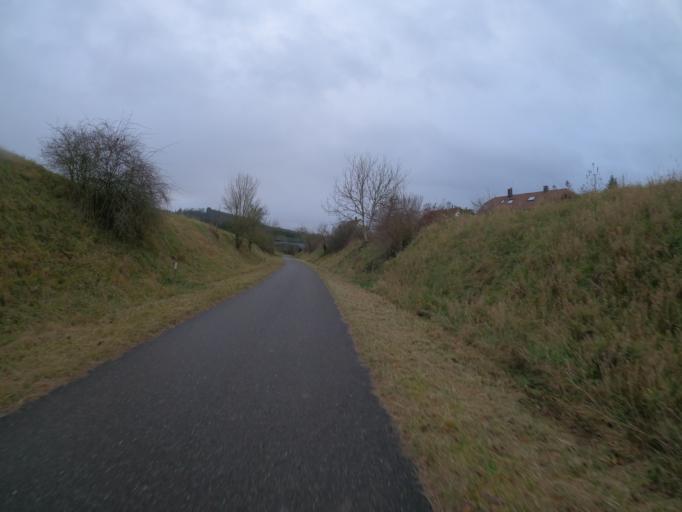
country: DE
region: Baden-Wuerttemberg
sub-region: Regierungsbezirk Stuttgart
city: Waschenbeuren
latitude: 48.7548
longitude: 9.6856
